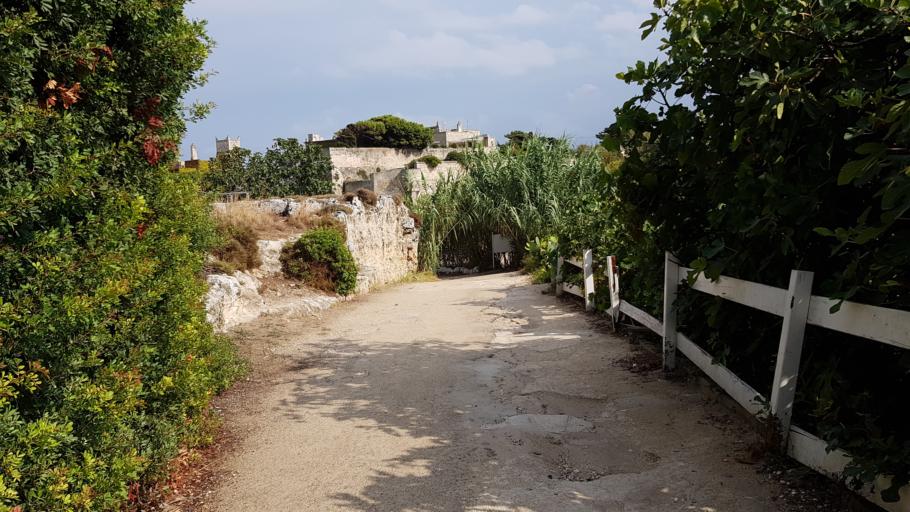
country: IT
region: Apulia
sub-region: Provincia di Bari
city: Monopoli
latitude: 40.9299
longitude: 17.3304
